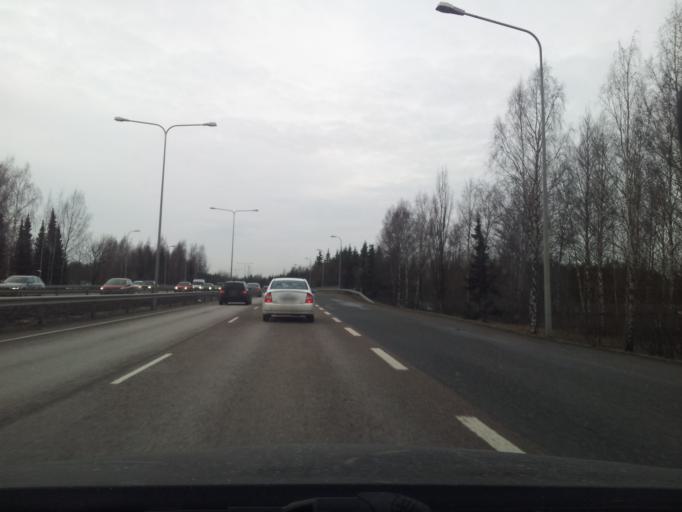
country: FI
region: Uusimaa
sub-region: Helsinki
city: Vantaa
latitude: 60.2431
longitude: 24.9752
